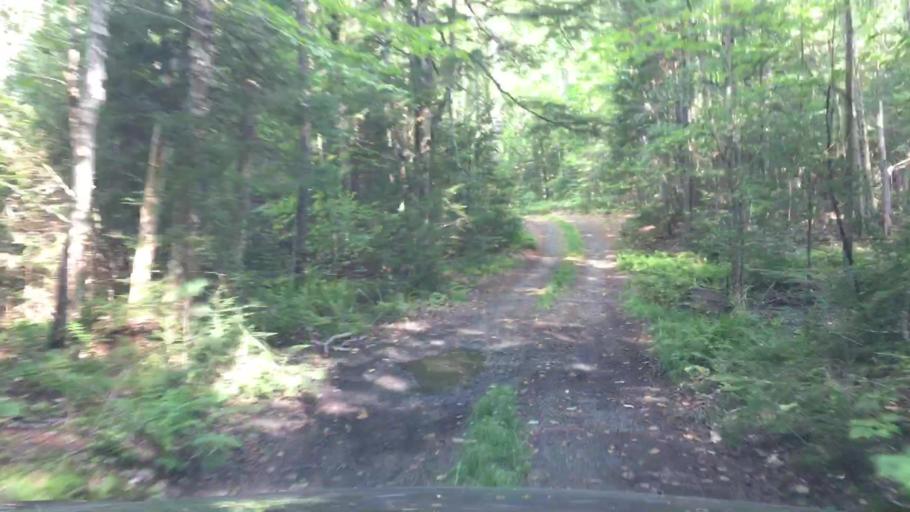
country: US
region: New Hampshire
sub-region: Grafton County
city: Littleton
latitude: 44.3047
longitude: -71.8961
